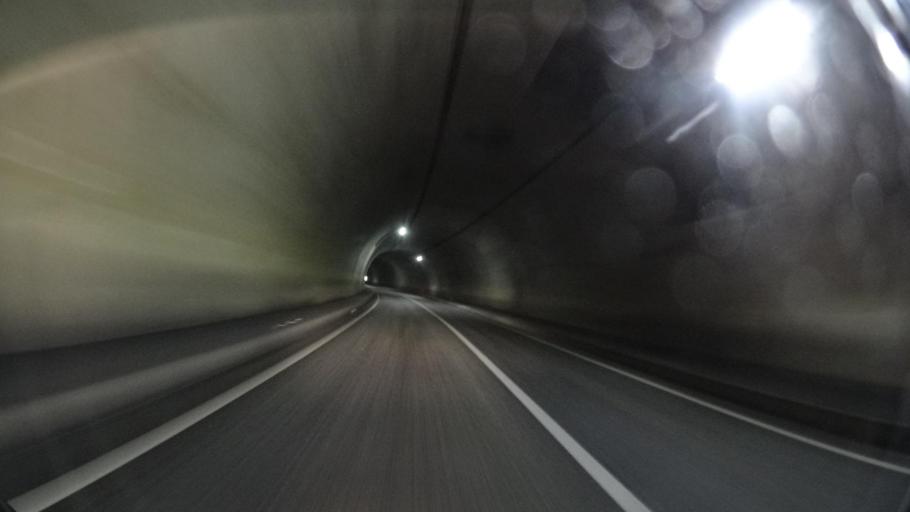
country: JP
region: Kyoto
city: Maizuru
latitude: 35.5239
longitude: 135.3455
